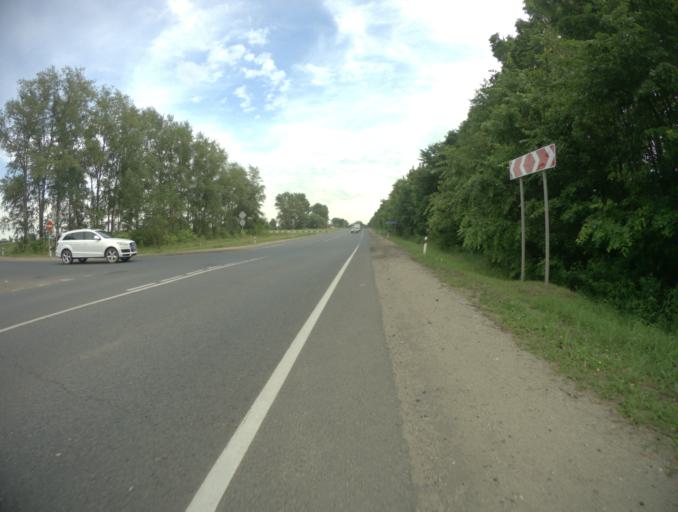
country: RU
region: Vladimir
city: Suzdal'
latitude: 56.3858
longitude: 40.4541
